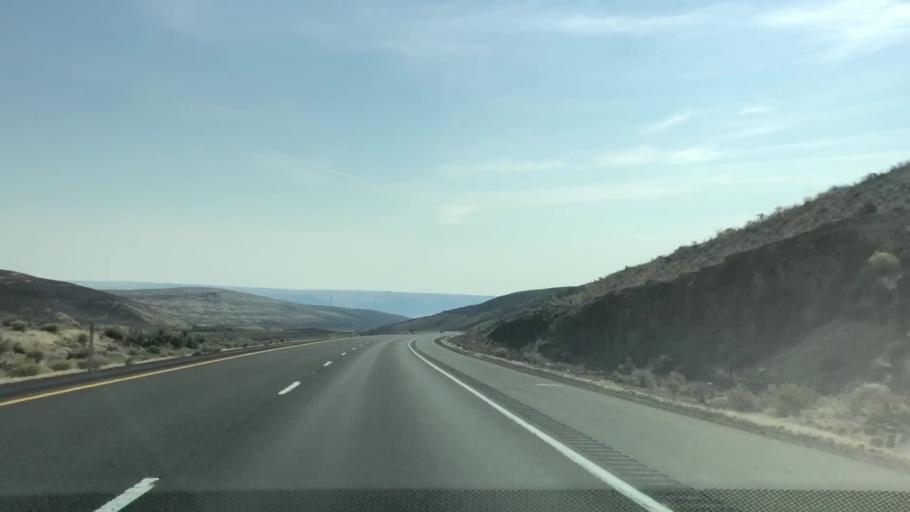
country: US
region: Washington
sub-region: Grant County
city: Mattawa
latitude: 46.9372
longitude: -120.0383
